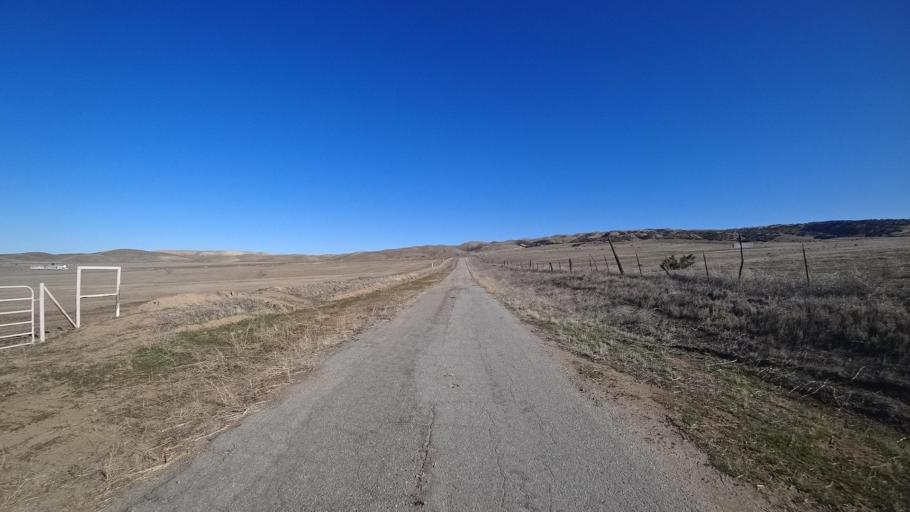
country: US
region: California
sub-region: Kern County
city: Maricopa
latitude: 34.9382
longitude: -119.4587
